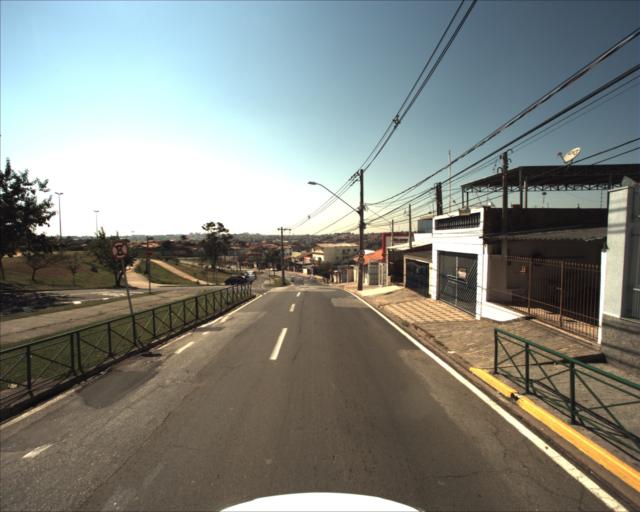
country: BR
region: Sao Paulo
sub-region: Sorocaba
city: Sorocaba
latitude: -23.5019
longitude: -47.5066
